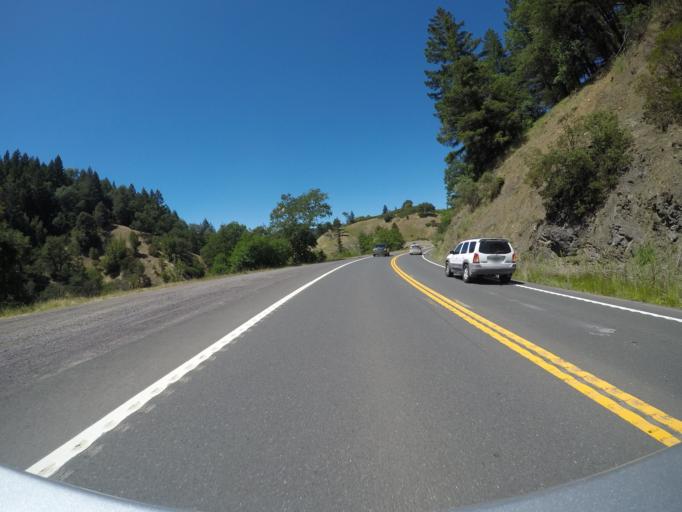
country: US
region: California
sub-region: Mendocino County
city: Laytonville
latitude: 39.7655
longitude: -123.5437
